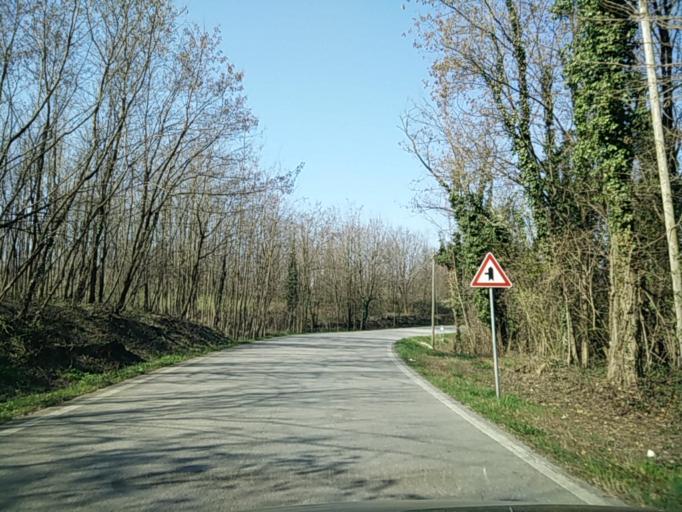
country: IT
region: Veneto
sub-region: Provincia di Treviso
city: Falze di Piave
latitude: 45.8393
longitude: 12.1850
